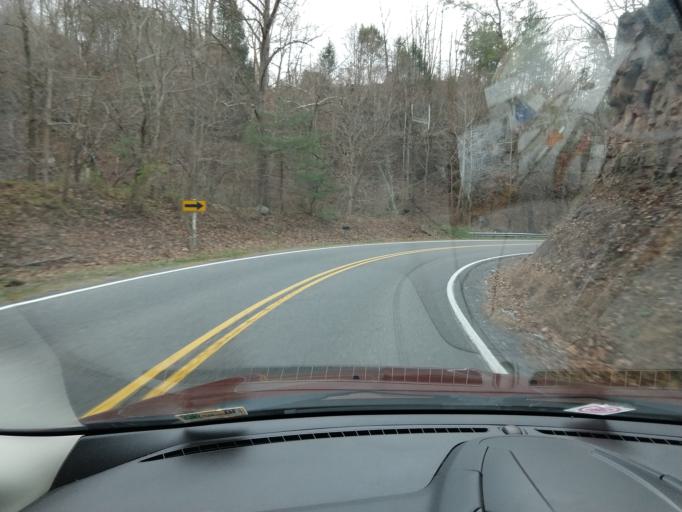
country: US
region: West Virginia
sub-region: Greenbrier County
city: White Sulphur Springs
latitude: 37.7335
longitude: -80.2261
